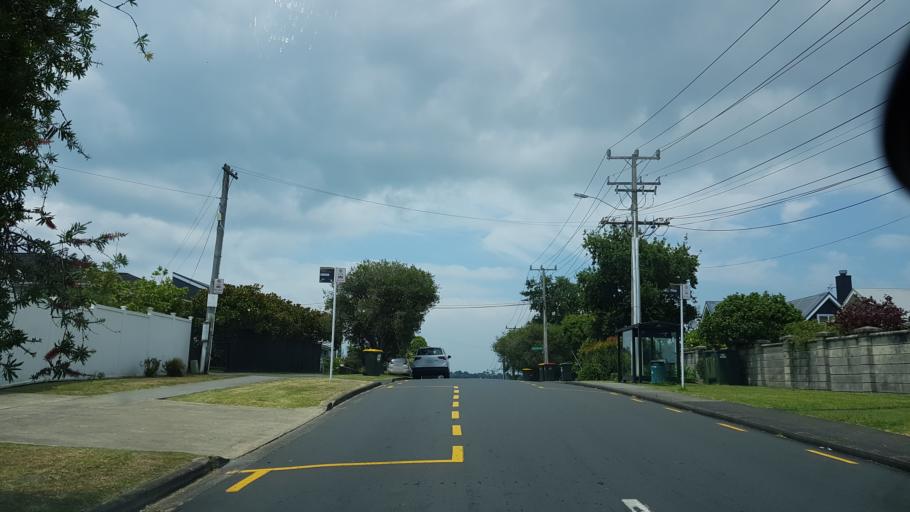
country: NZ
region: Auckland
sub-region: Auckland
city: North Shore
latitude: -36.7995
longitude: 174.7777
